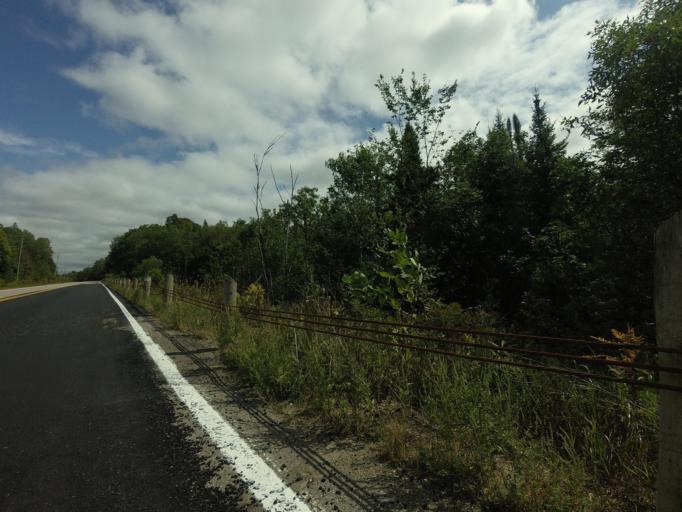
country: CA
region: Ontario
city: Omemee
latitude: 44.8774
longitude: -78.5139
